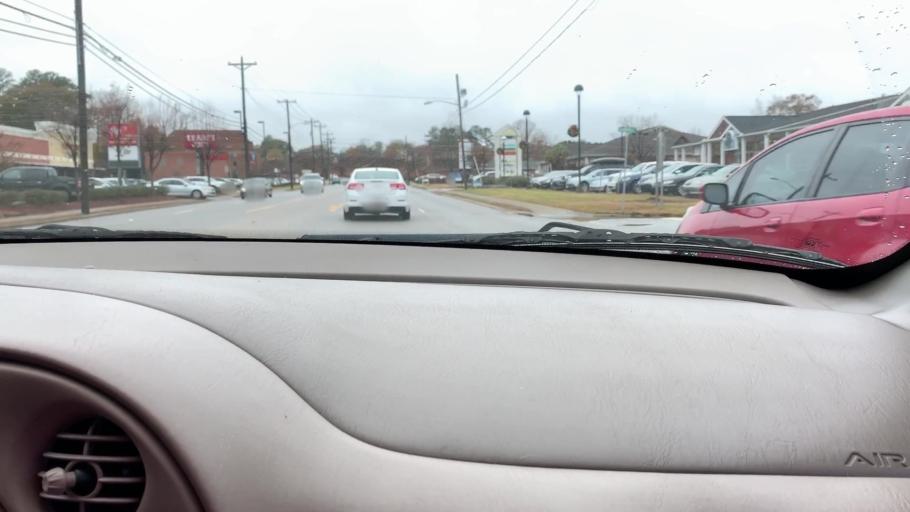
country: US
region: South Carolina
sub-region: Richland County
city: Forest Acres
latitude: 34.0202
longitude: -80.9716
